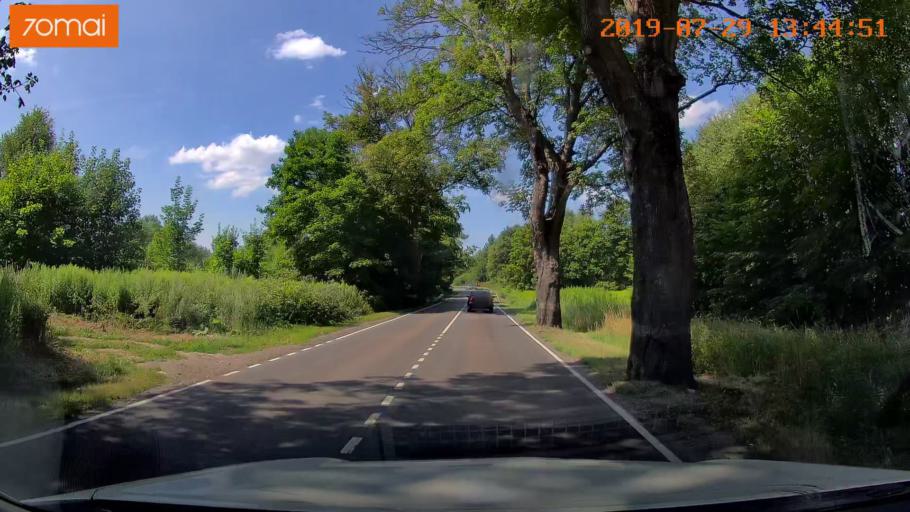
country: RU
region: Kaliningrad
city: Primorsk
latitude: 54.7388
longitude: 20.0825
